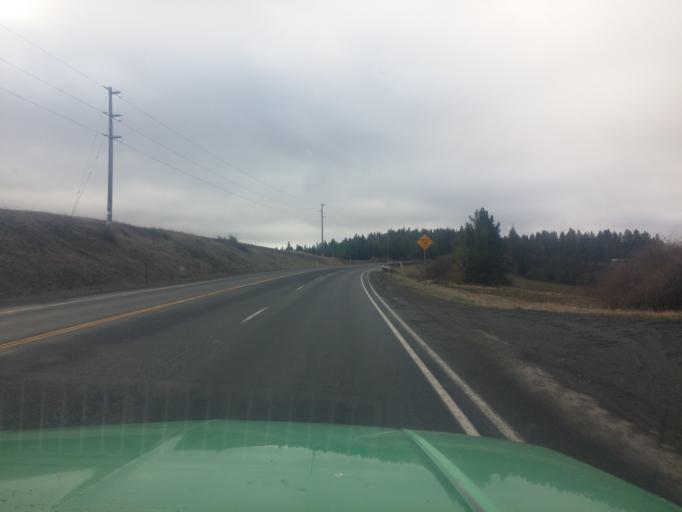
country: US
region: Idaho
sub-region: Latah County
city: Moscow
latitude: 46.8819
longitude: -117.0034
